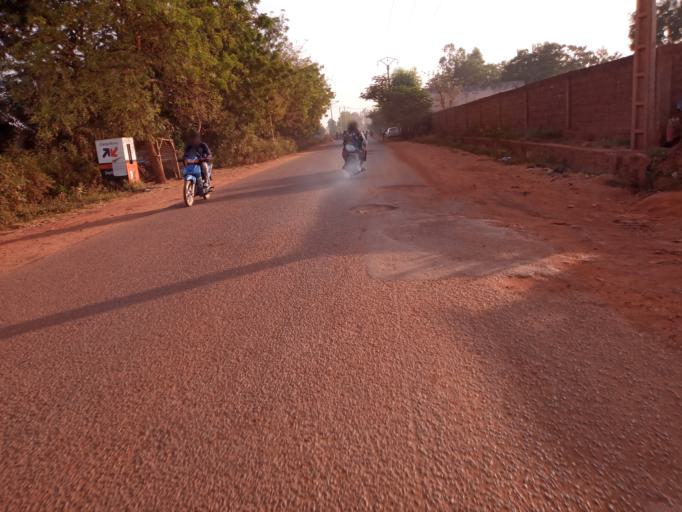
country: ML
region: Bamako
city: Bamako
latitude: 12.6325
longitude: -7.9407
